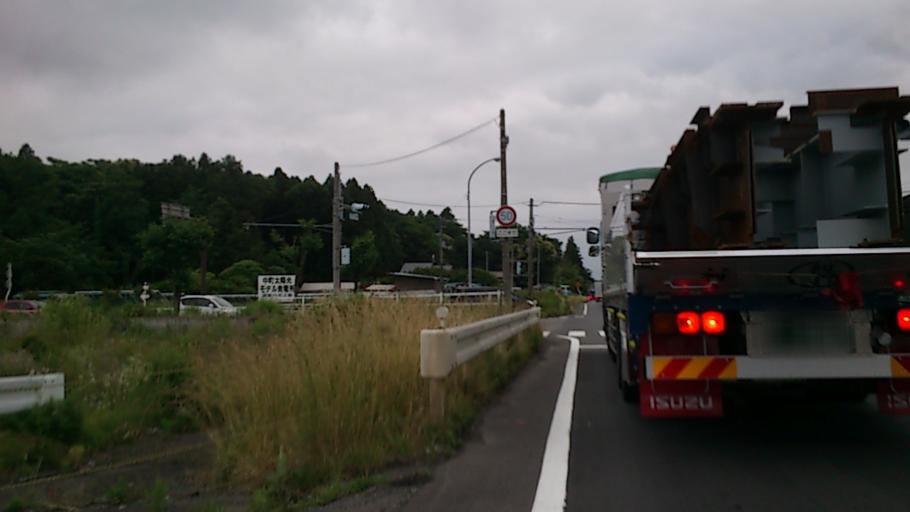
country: JP
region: Fukushima
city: Sukagawa
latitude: 37.2481
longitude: 140.3380
